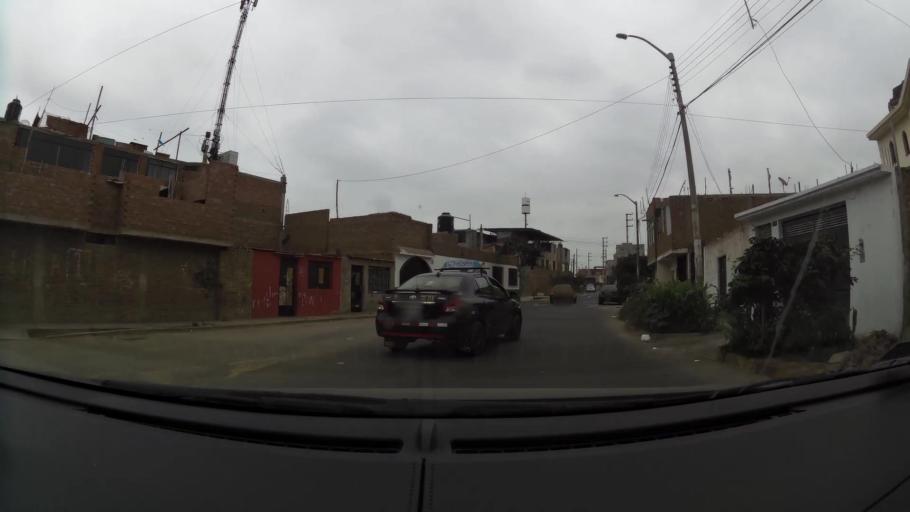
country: PE
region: La Libertad
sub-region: Provincia de Trujillo
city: Trujillo
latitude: -8.1062
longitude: -79.0441
